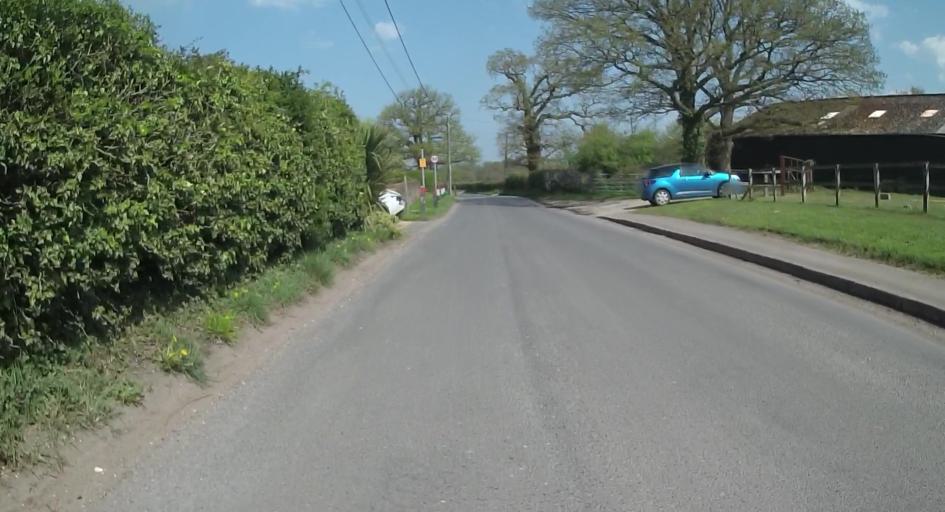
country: GB
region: England
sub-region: Hampshire
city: Basingstoke
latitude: 51.2974
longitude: -1.1006
